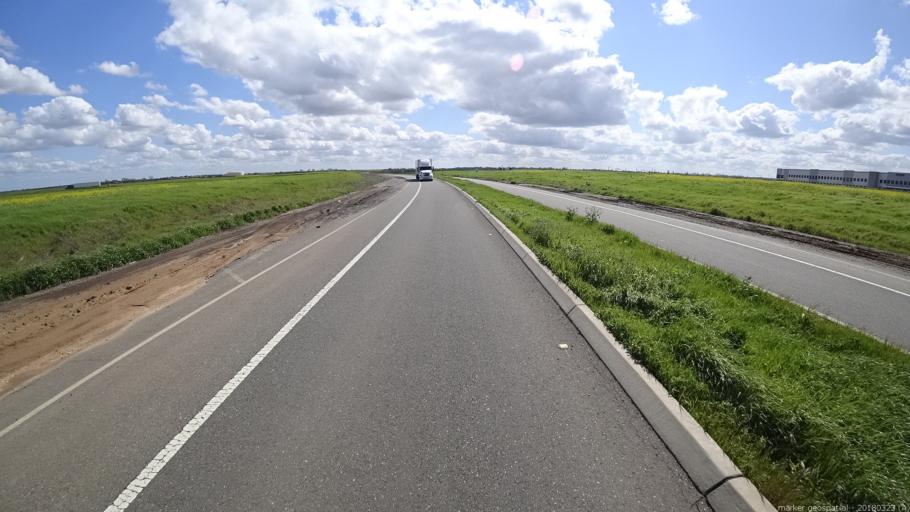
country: US
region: California
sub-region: Yolo County
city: West Sacramento
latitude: 38.6840
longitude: -121.5695
